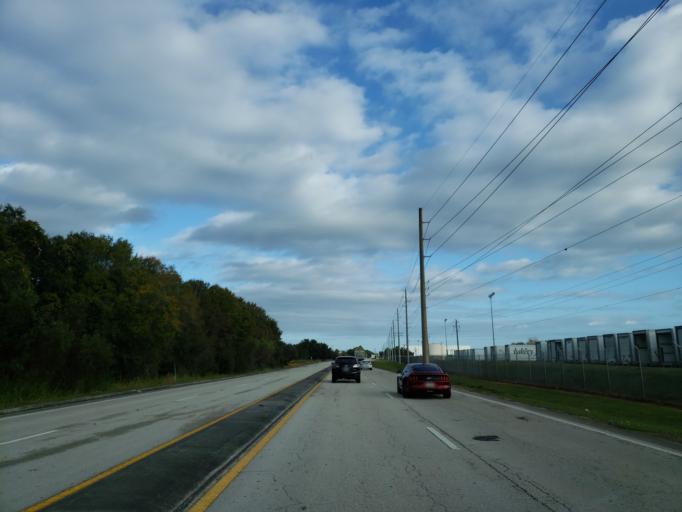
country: US
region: Florida
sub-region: Hillsborough County
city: Plant City
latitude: 27.9919
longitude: -82.1049
